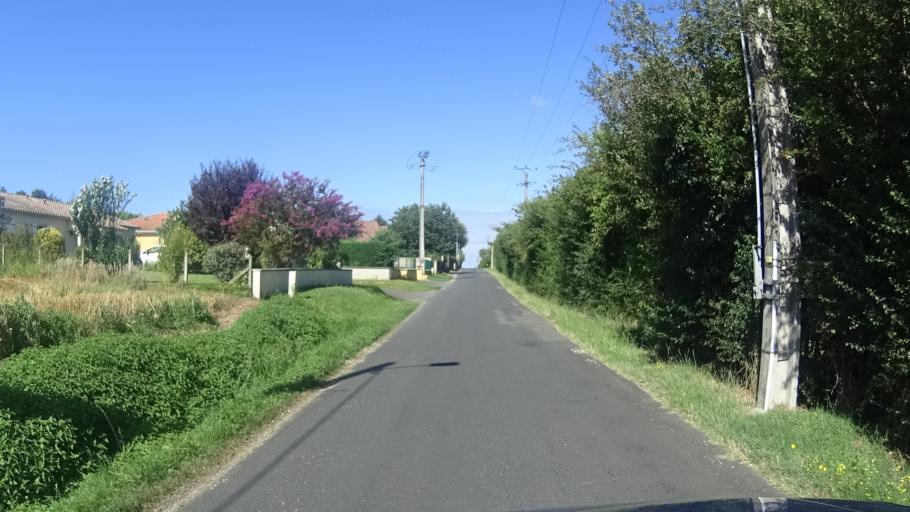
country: FR
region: Aquitaine
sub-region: Departement de la Dordogne
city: Mussidan
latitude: 45.0333
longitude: 0.3811
